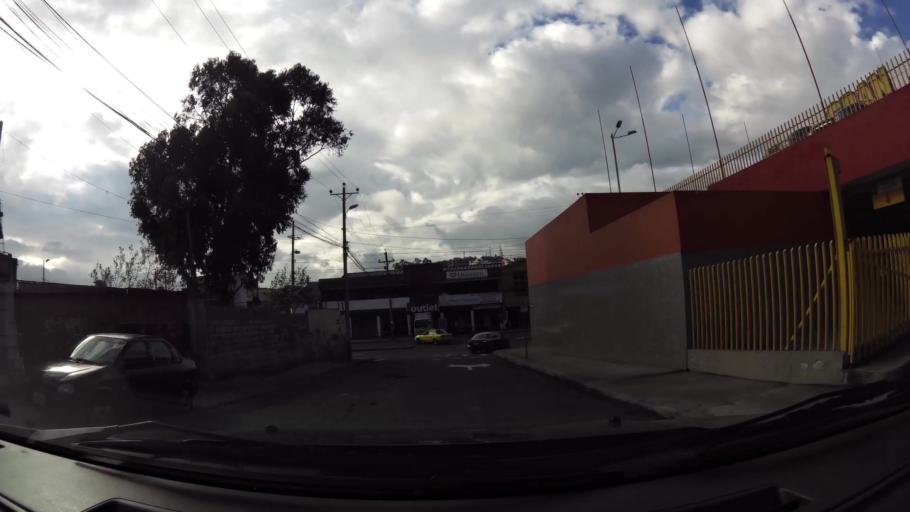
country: EC
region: Pichincha
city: Quito
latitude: -0.1292
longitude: -78.4726
